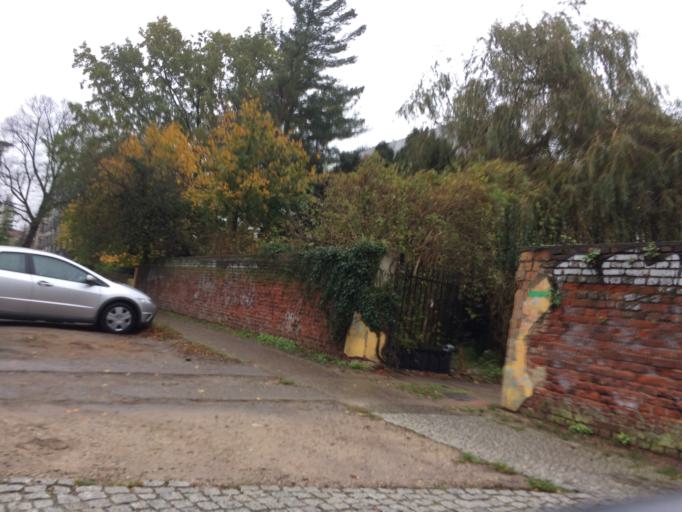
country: DE
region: Berlin
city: Niederschonhausen
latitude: 52.5794
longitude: 13.4047
